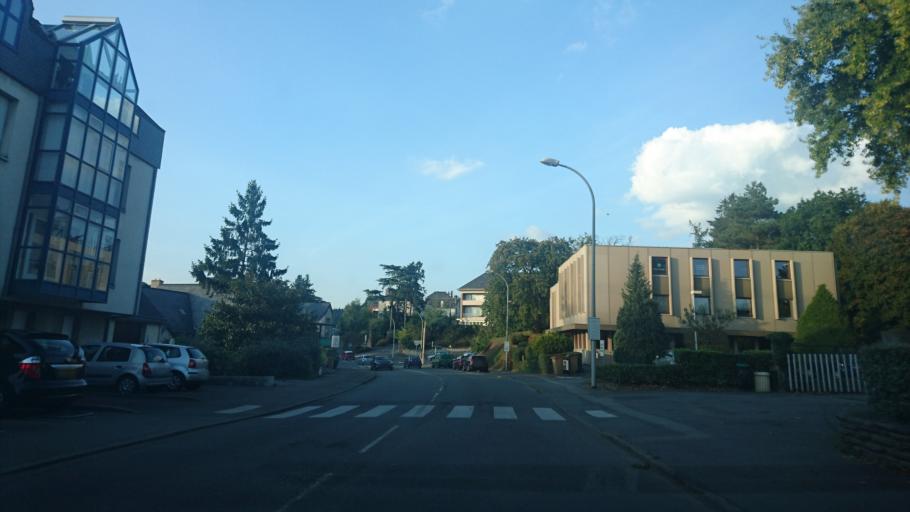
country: FR
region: Brittany
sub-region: Departement d'Ille-et-Vilaine
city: Redon
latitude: 47.6544
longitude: -2.0831
